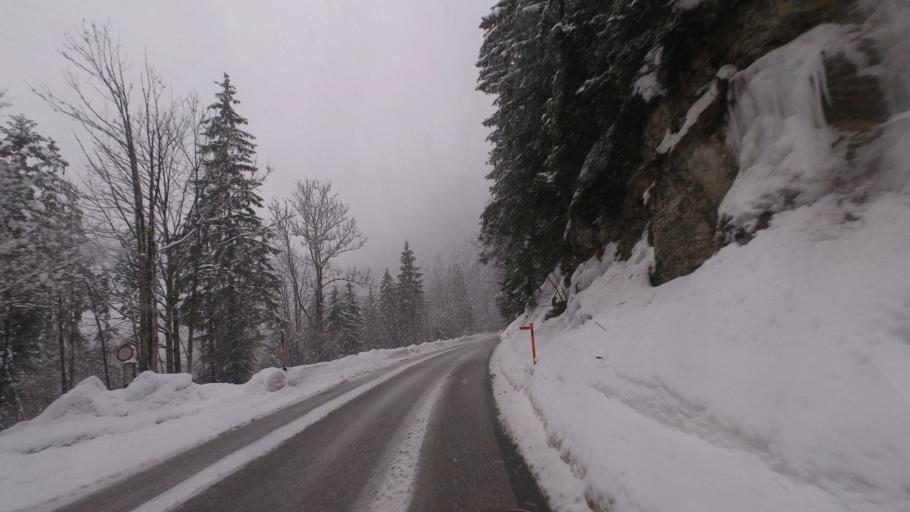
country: AT
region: Tyrol
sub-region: Politischer Bezirk Kitzbuhel
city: Kossen
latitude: 47.6875
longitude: 12.3961
